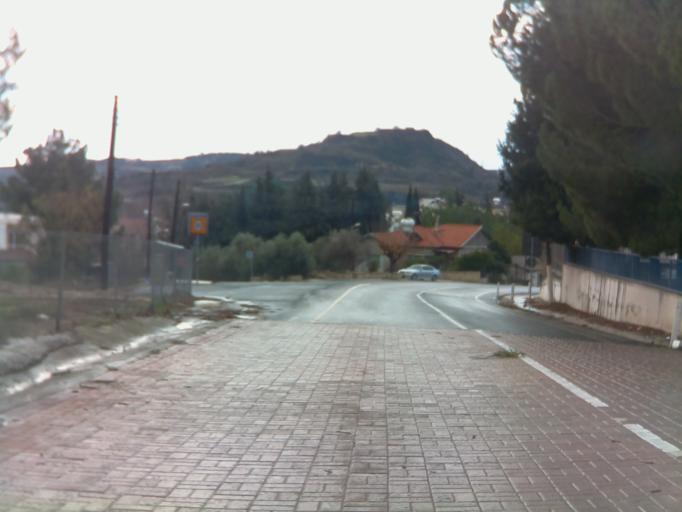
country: CY
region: Pafos
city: Tala
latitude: 34.8840
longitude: 32.4825
